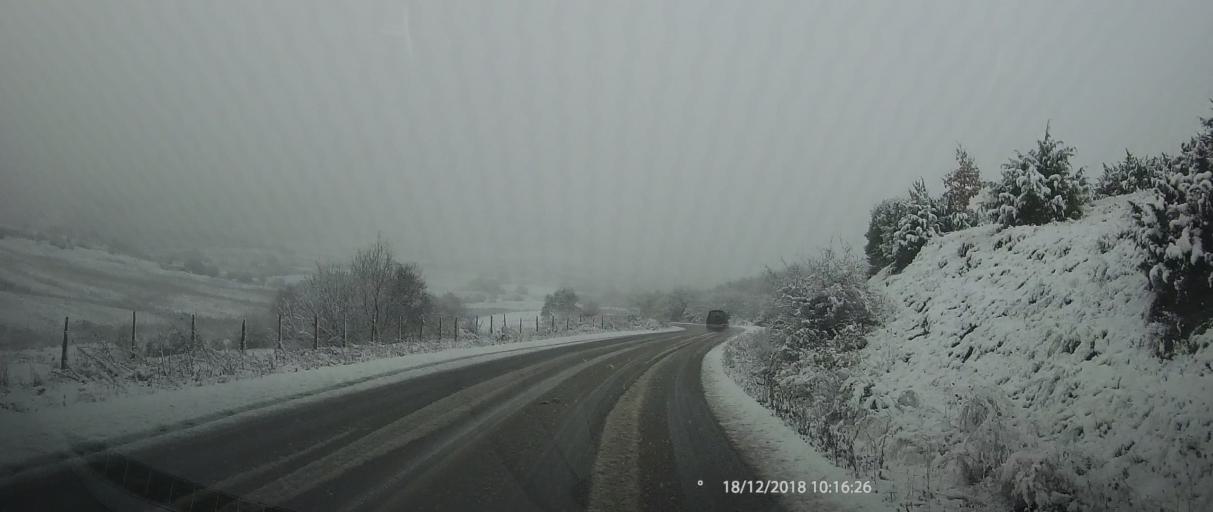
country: GR
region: Thessaly
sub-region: Nomos Larisis
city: Livadi
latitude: 40.1159
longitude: 22.2102
